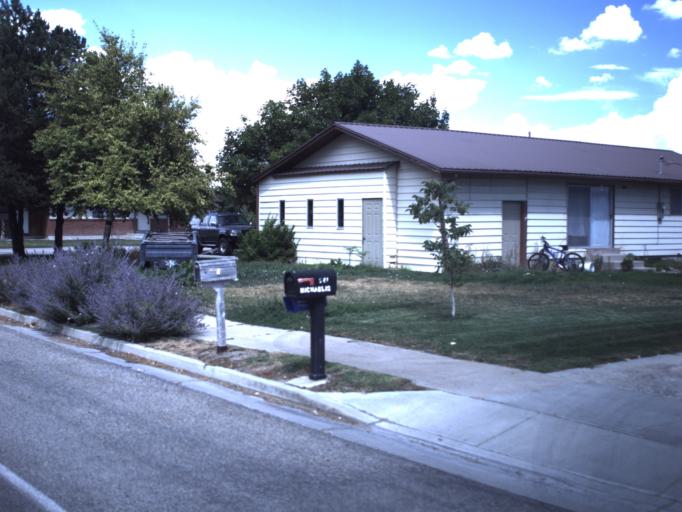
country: US
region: Utah
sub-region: Box Elder County
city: Garland
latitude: 41.7353
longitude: -112.1625
